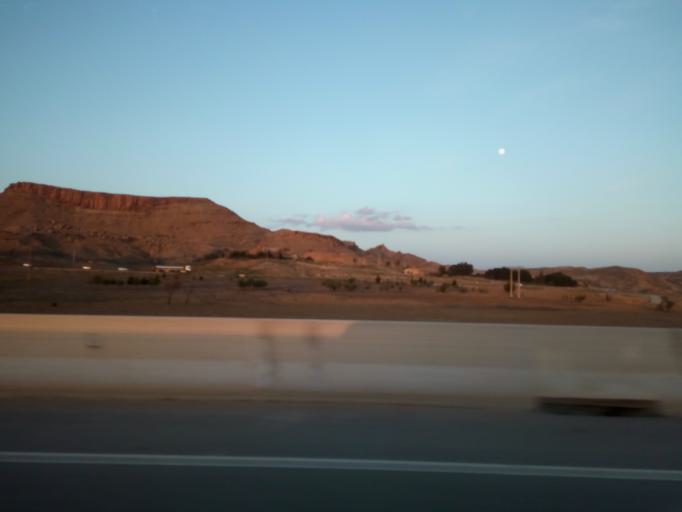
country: DZ
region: Medea
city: Ksar el Boukhari
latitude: 35.8117
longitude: 2.7665
